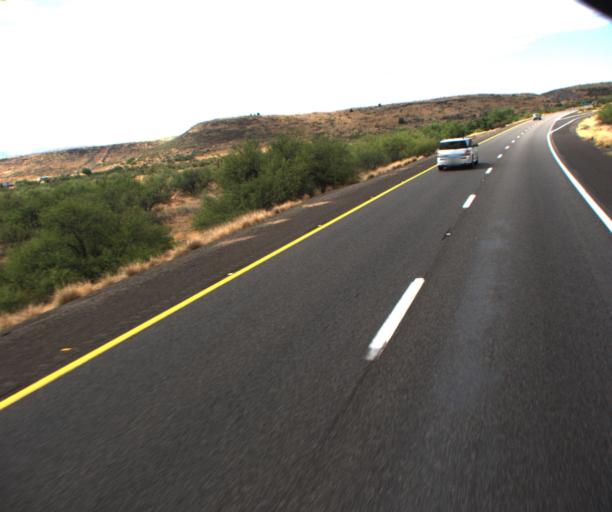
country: US
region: Arizona
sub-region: Yavapai County
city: Cordes Lakes
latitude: 34.2411
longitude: -112.1144
